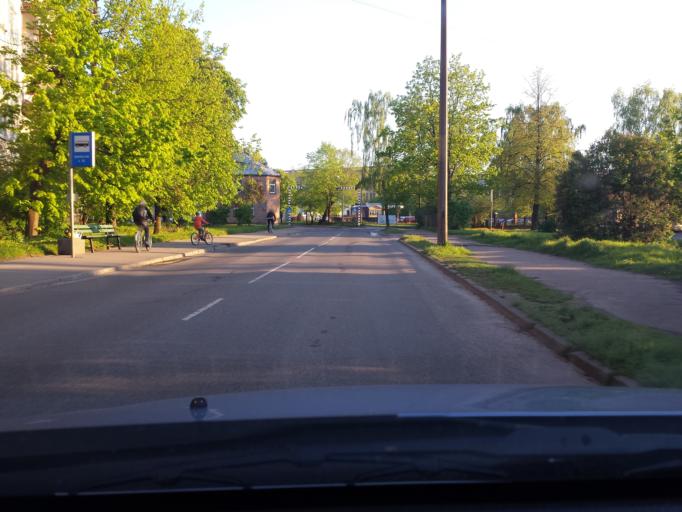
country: LV
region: Riga
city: Riga
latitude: 56.9995
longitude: 24.1180
